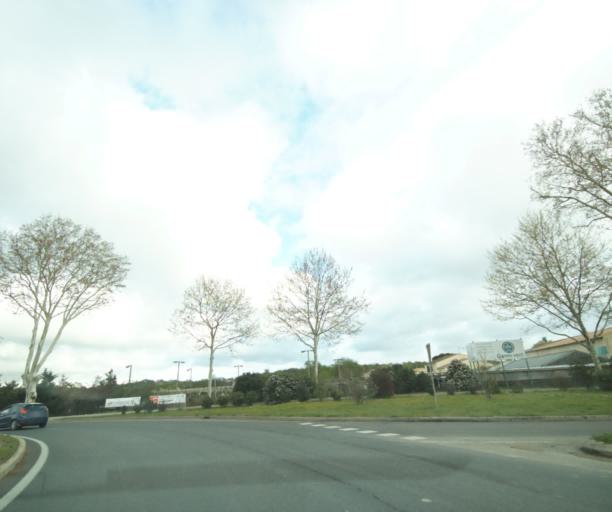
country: FR
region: Languedoc-Roussillon
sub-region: Departement de l'Herault
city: Laverune
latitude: 43.5874
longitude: 3.8102
